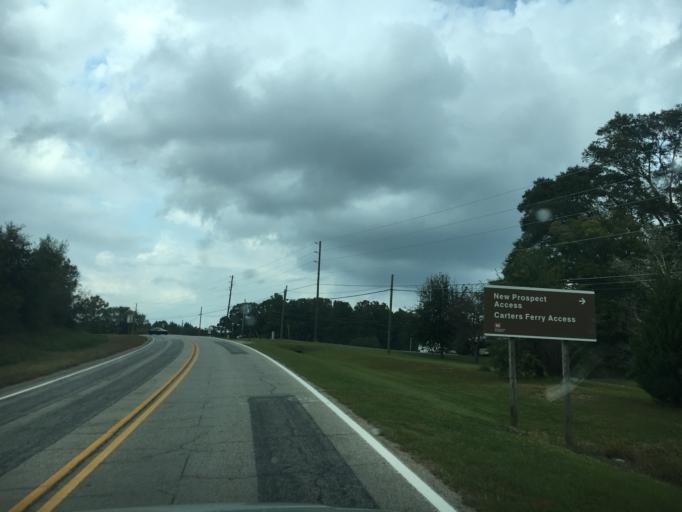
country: US
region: Georgia
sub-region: Hart County
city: Reed Creek
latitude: 34.4036
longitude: -82.9295
